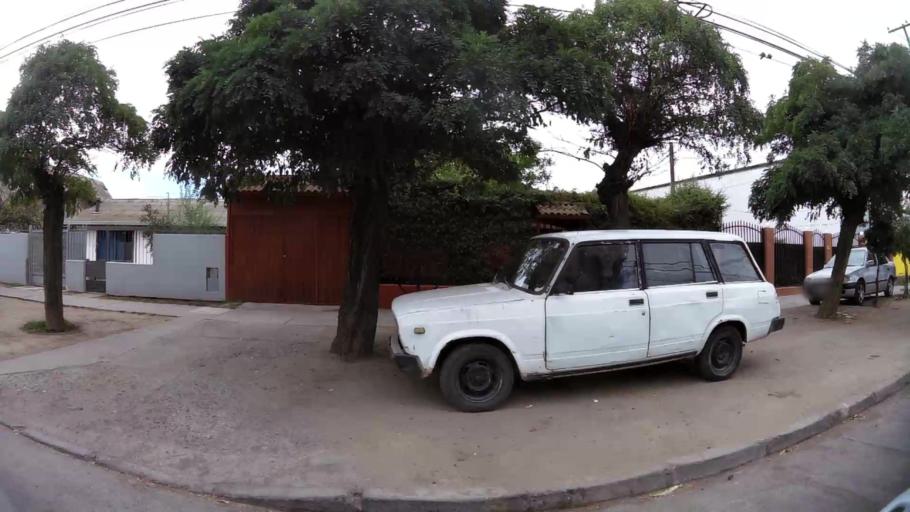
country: CL
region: O'Higgins
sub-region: Provincia de Cachapoal
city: Rancagua
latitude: -34.1503
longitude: -70.7363
